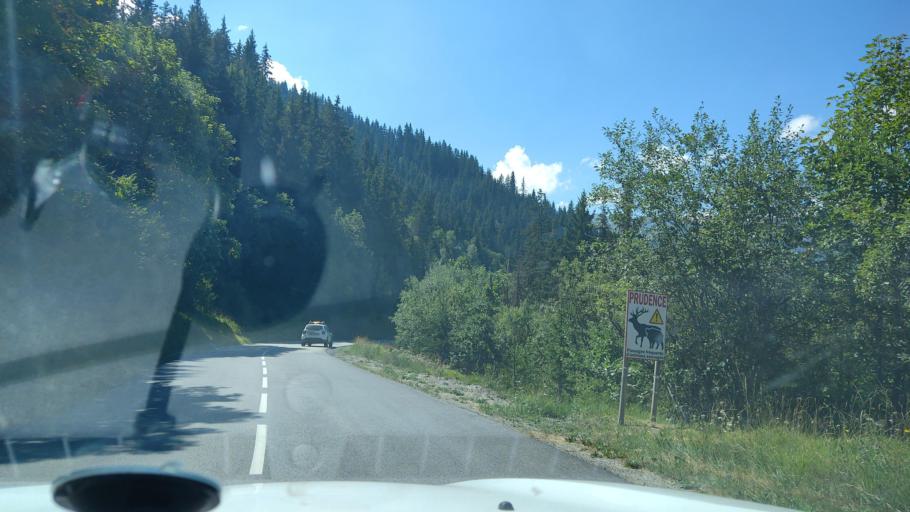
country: FR
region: Rhone-Alpes
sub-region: Departement de la Savoie
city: Les Allues
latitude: 45.4326
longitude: 6.5756
